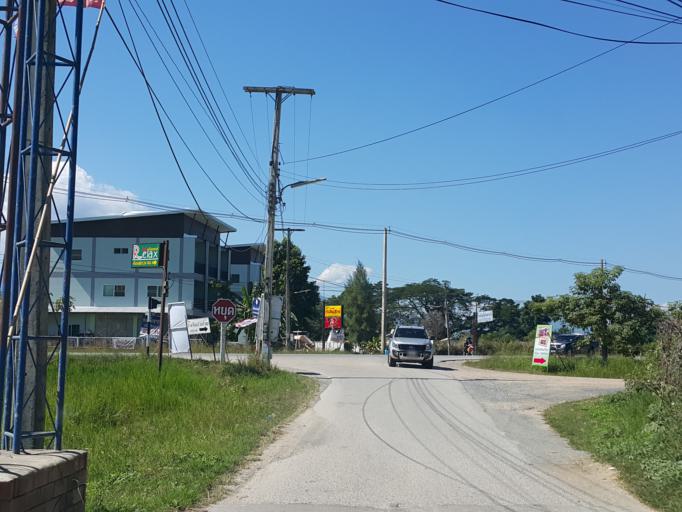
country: TH
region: Chiang Mai
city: San Sai
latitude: 18.8177
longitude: 99.0533
